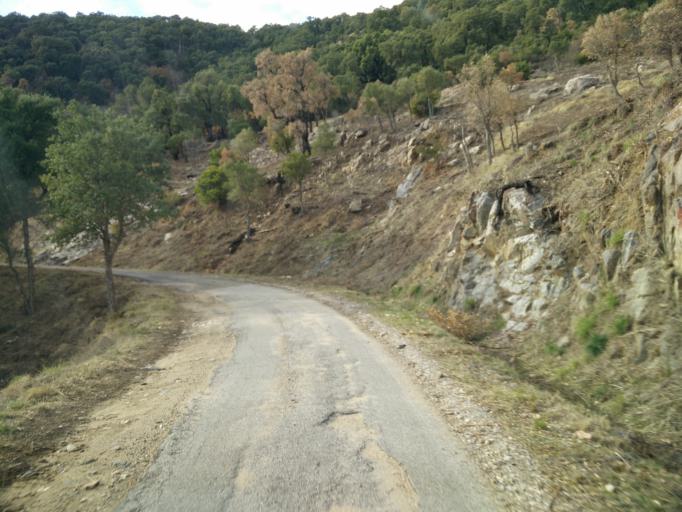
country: FR
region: Provence-Alpes-Cote d'Azur
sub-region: Departement du Var
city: Roquebrune-sur-Argens
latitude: 43.4077
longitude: 6.6304
